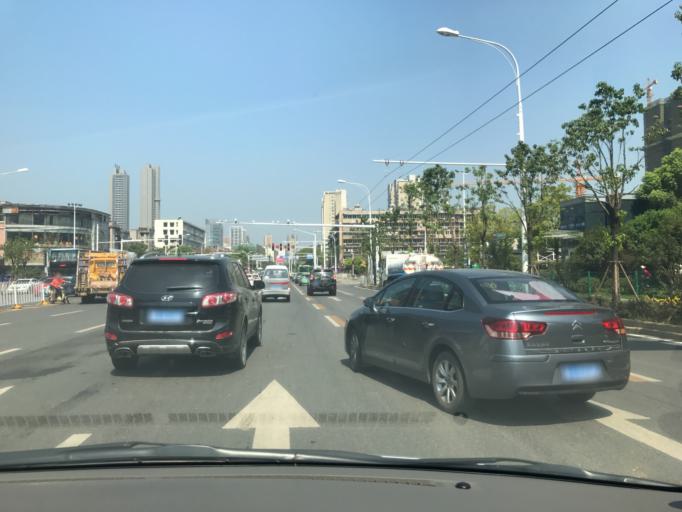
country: CN
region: Hubei
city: Shilipu
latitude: 30.5616
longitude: 114.2149
